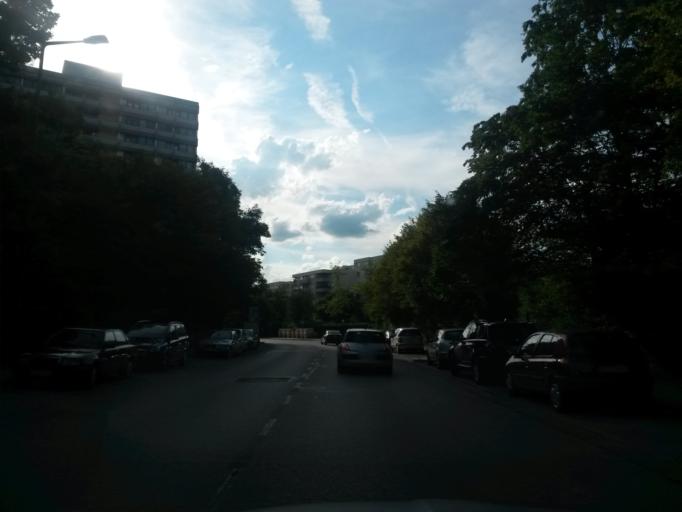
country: DE
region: Bavaria
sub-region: Upper Bavaria
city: Neubiberg
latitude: 48.0982
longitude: 11.6514
